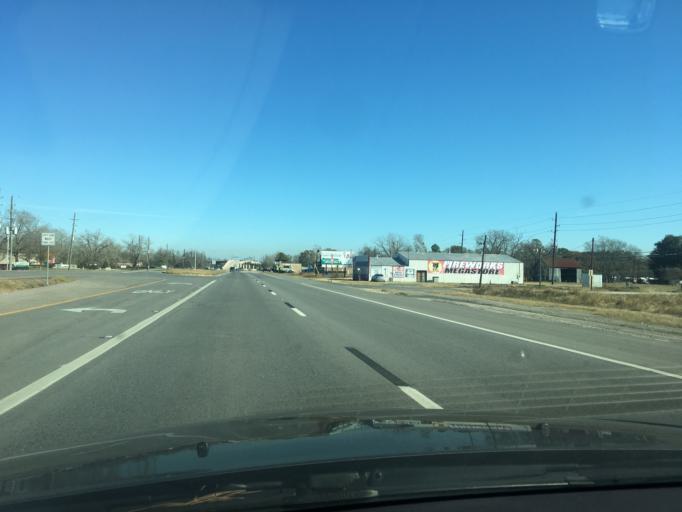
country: US
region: Texas
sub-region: Fort Bend County
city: Richmond
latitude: 29.5889
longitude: -95.7486
